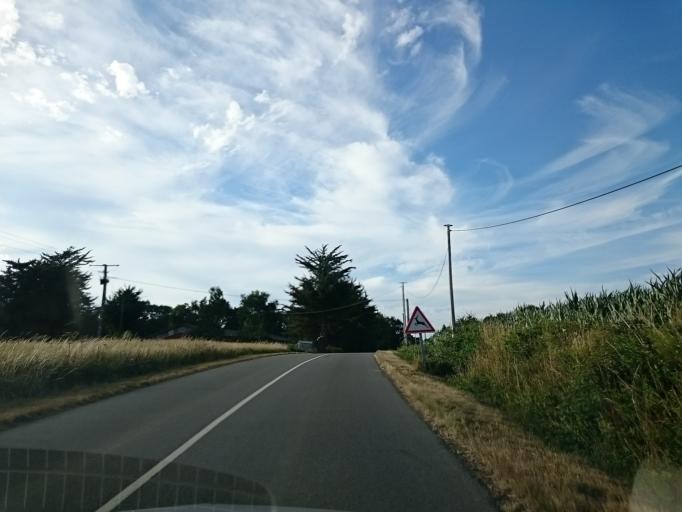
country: FR
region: Brittany
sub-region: Departement d'Ille-et-Vilaine
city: Pance
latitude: 47.9035
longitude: -1.6166
